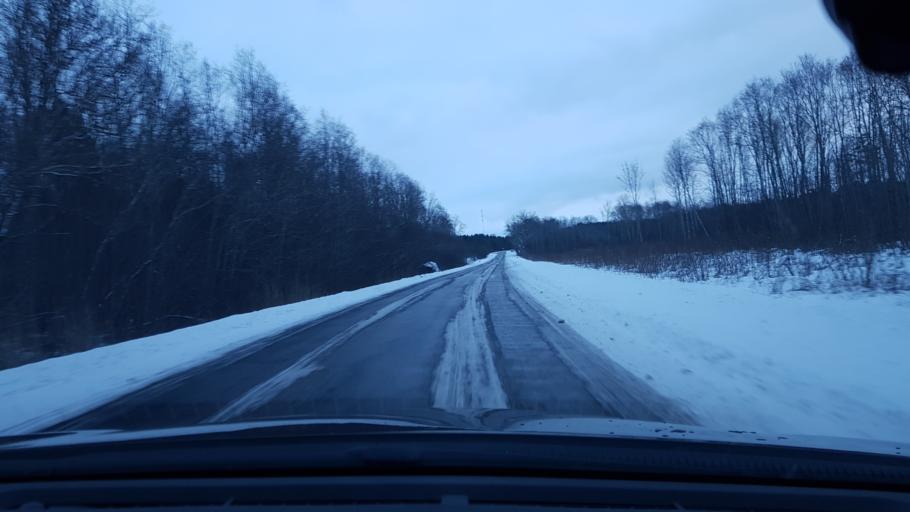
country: EE
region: Laeaene
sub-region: Ridala Parish
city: Uuemoisa
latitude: 59.0709
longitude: 23.5776
